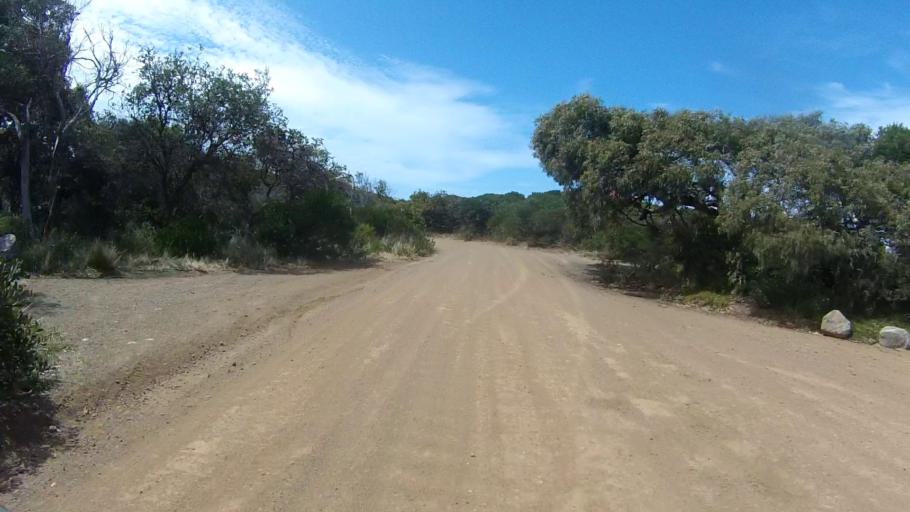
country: AU
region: Tasmania
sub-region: Clarence
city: Sandford
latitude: -43.0258
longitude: 147.4850
